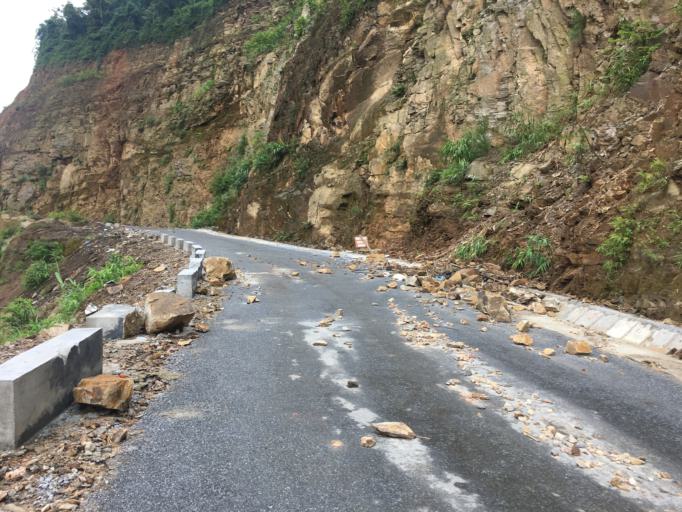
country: VN
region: Ha Giang
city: Thi Tran Tam Son
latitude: 22.9803
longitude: 105.0563
